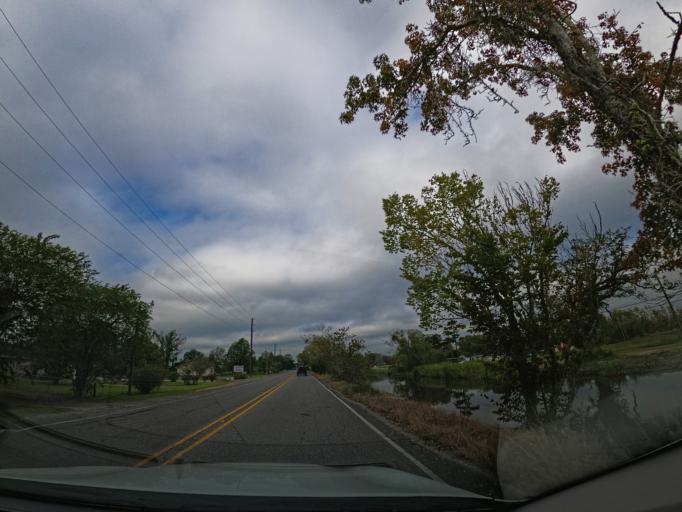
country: US
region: Louisiana
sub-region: Terrebonne Parish
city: Bayou Cane
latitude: 29.6063
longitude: -90.8712
